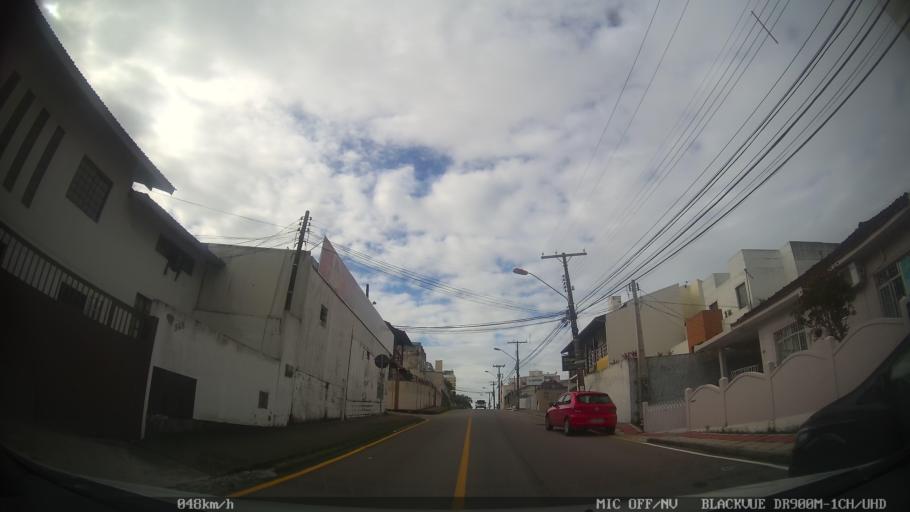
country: BR
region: Santa Catarina
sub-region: Sao Jose
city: Campinas
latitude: -27.5711
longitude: -48.6111
